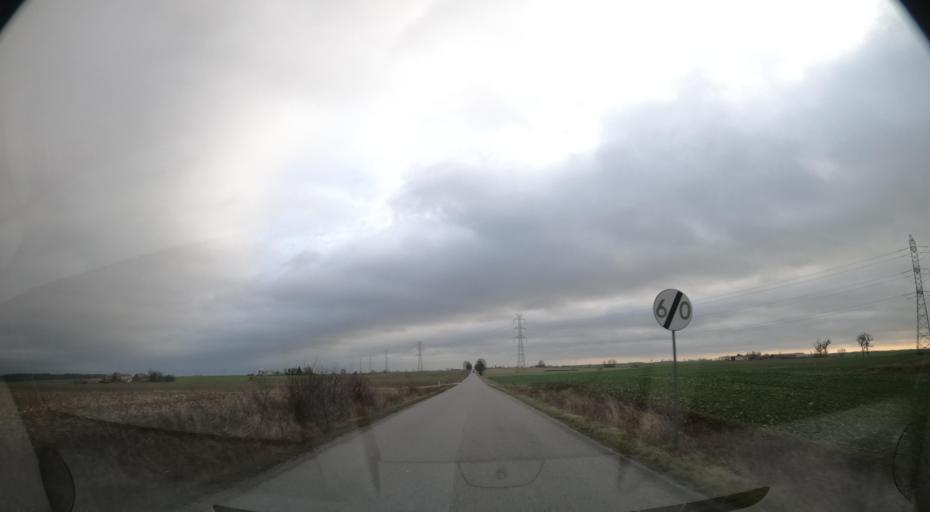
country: PL
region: Kujawsko-Pomorskie
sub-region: Powiat nakielski
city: Sadki
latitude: 53.1806
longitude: 17.4078
